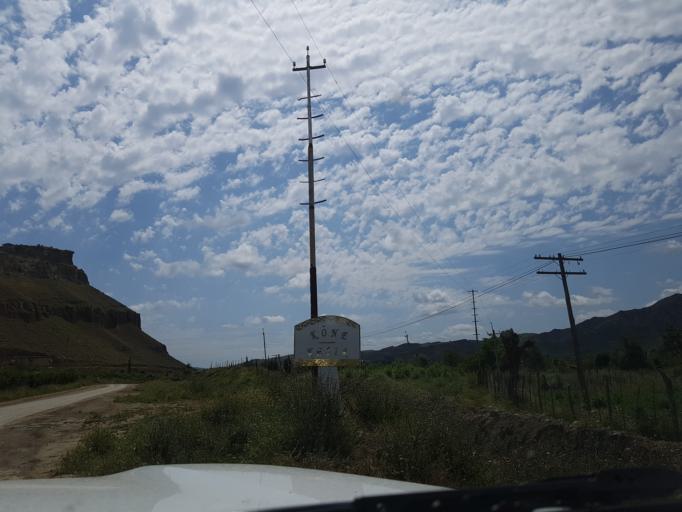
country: TM
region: Ahal
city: Baharly
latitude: 38.2228
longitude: 56.8976
